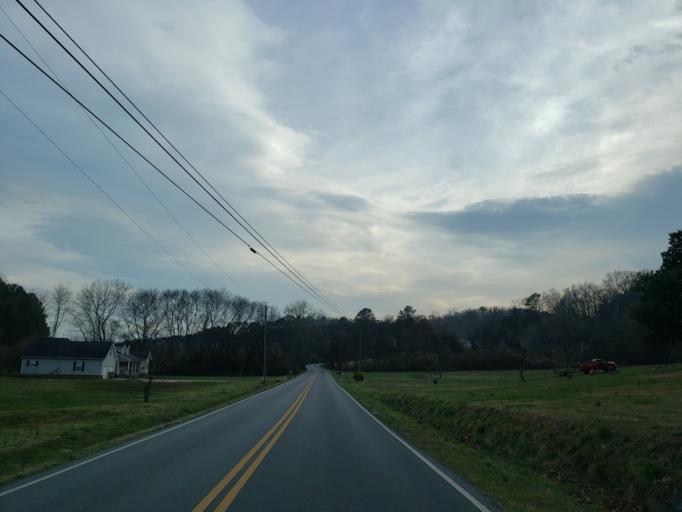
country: US
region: Georgia
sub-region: Whitfield County
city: Varnell
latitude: 34.9019
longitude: -84.9616
